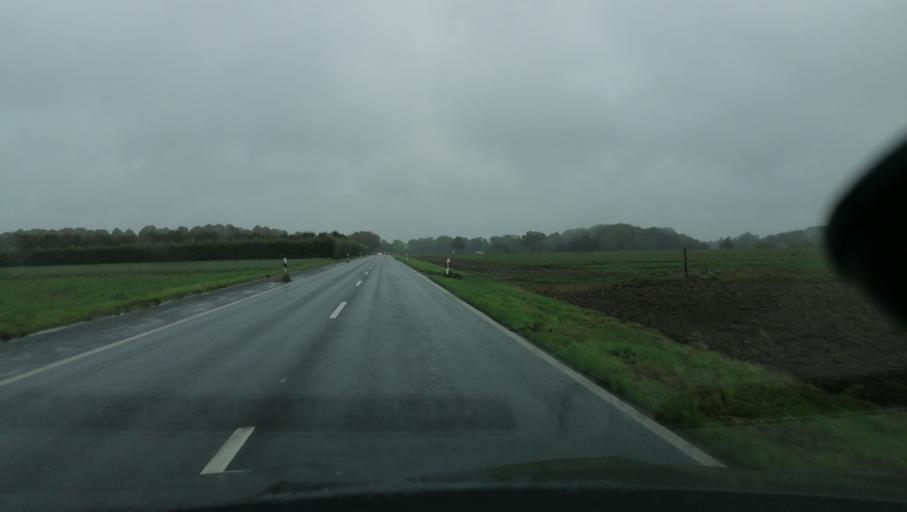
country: DE
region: North Rhine-Westphalia
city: Oer-Erkenschwick
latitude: 51.6241
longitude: 7.2921
